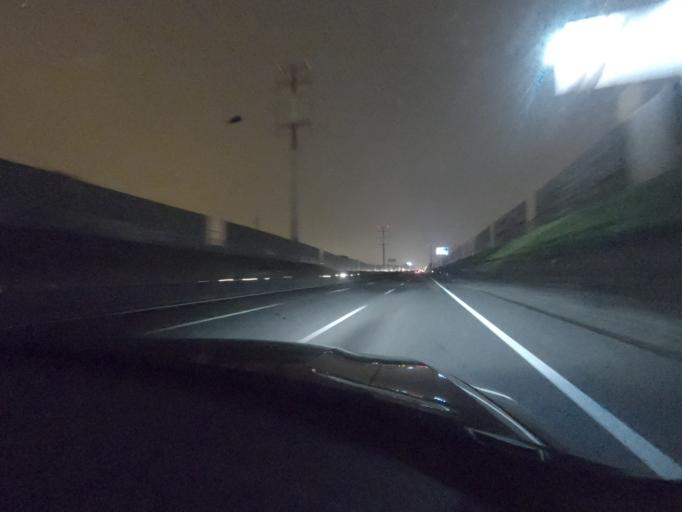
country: PT
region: Lisbon
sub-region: Loures
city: Sao Joao da Talha
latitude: 38.8343
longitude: -9.0964
